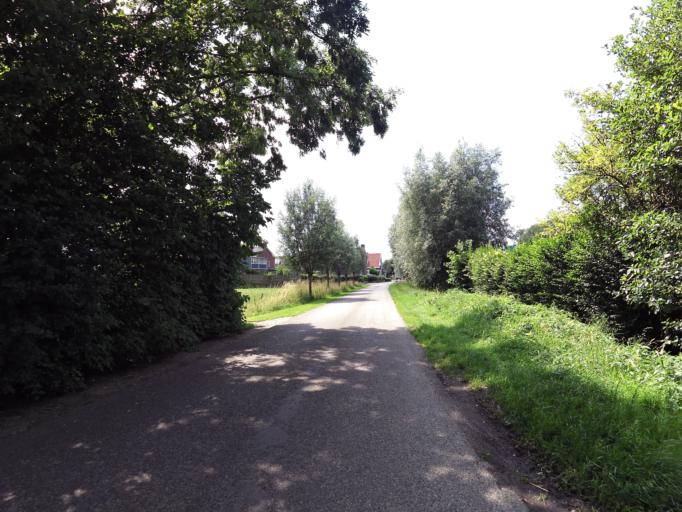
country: NL
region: Gelderland
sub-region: Gemeente Doesburg
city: Doesburg
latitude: 51.9553
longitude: 6.1413
